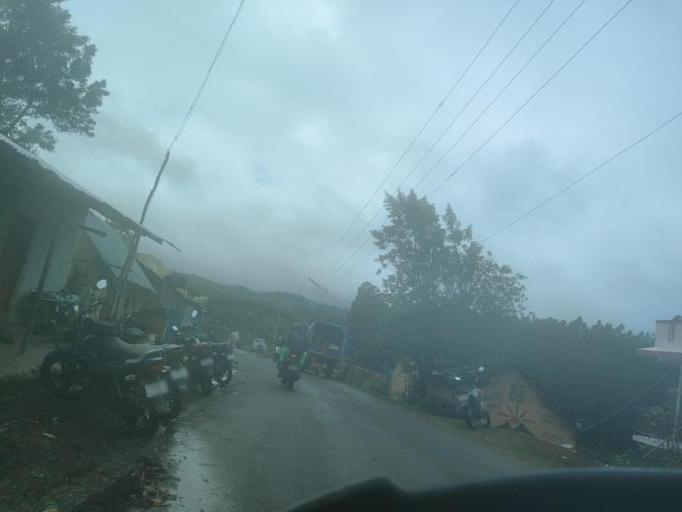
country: IN
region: Tamil Nadu
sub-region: Dindigul
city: Kodaikanal
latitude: 10.2270
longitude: 77.3519
